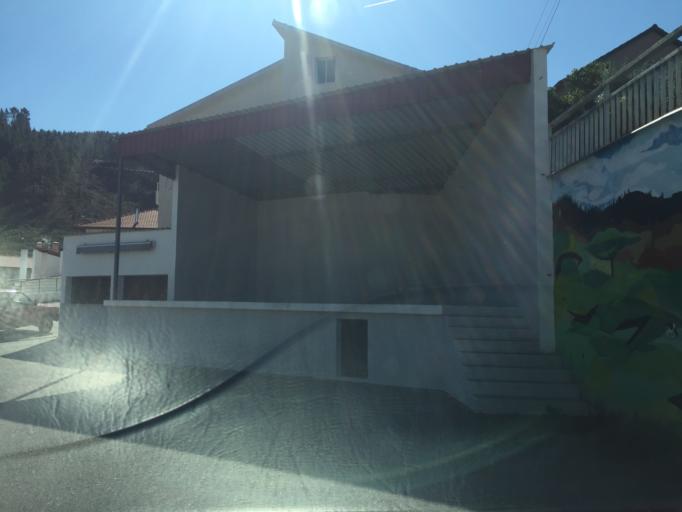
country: PT
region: Coimbra
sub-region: Pampilhosa da Serra
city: Pampilhosa da Serra
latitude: 40.0834
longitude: -7.7852
